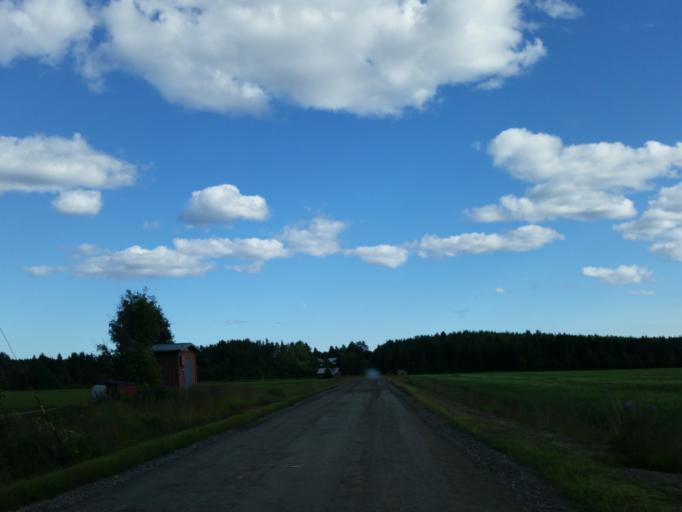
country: SE
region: Vaesterbotten
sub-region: Robertsfors Kommun
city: Robertsfors
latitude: 64.1282
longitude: 20.8884
